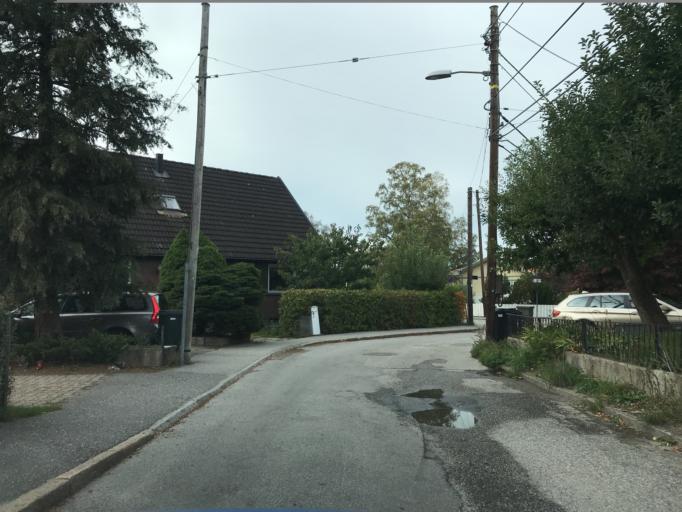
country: SE
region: Stockholm
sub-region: Huddinge Kommun
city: Segeltorp
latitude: 59.2760
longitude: 17.9663
